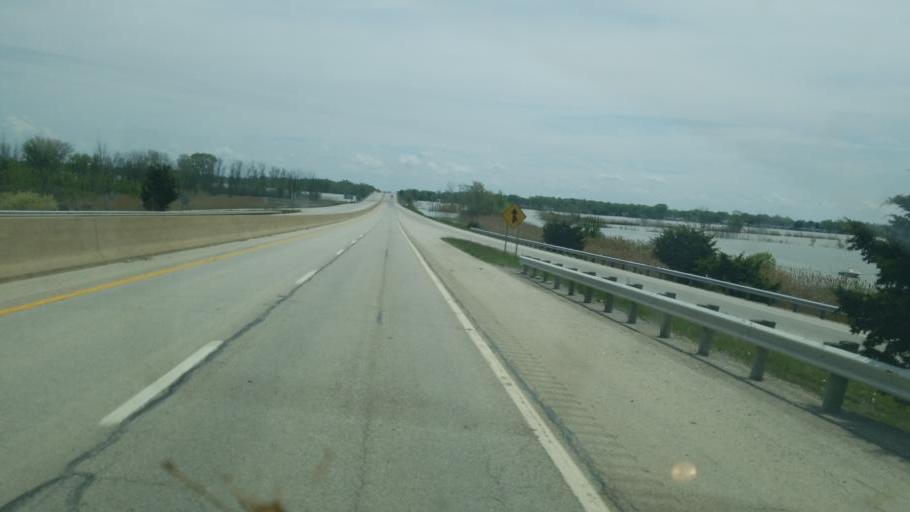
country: US
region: Ohio
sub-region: Ottawa County
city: Port Clinton
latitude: 41.5179
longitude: -82.9997
